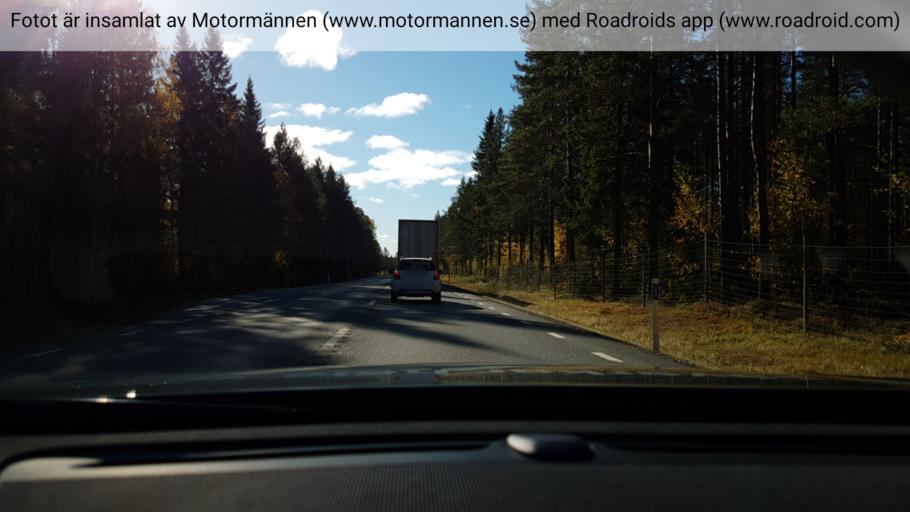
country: SE
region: Vaesterbotten
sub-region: Skelleftea Kommun
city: Burea
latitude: 64.5280
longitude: 21.2579
